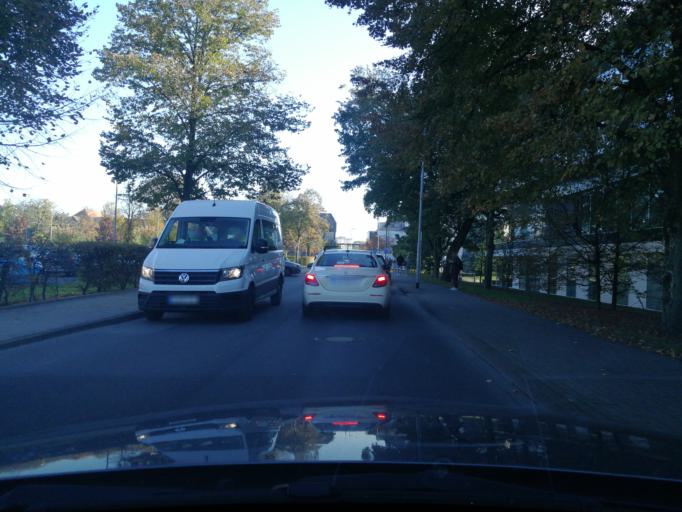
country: DE
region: North Rhine-Westphalia
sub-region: Regierungsbezirk Dusseldorf
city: Dusseldorf
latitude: 51.1966
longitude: 6.7885
